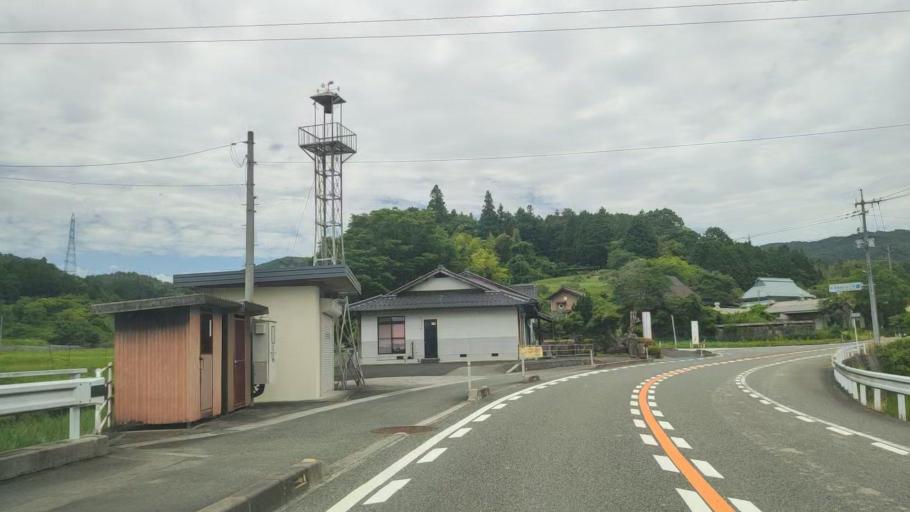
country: JP
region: Okayama
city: Tsuyama
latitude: 35.0794
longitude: 134.2475
